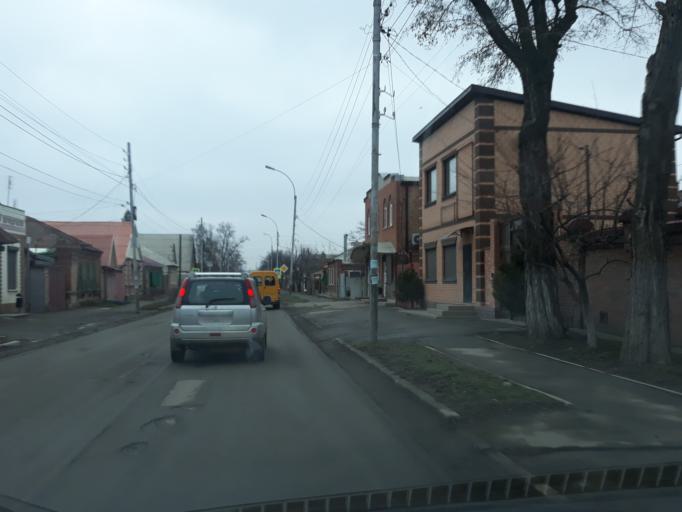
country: RU
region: Rostov
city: Taganrog
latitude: 47.2262
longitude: 38.9241
